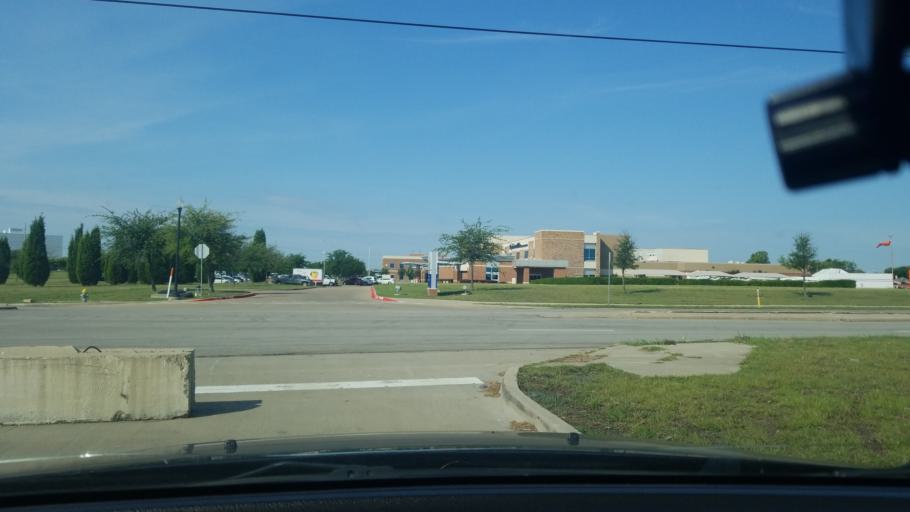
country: US
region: Texas
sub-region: Dallas County
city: Sunnyvale
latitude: 32.7804
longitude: -96.5672
